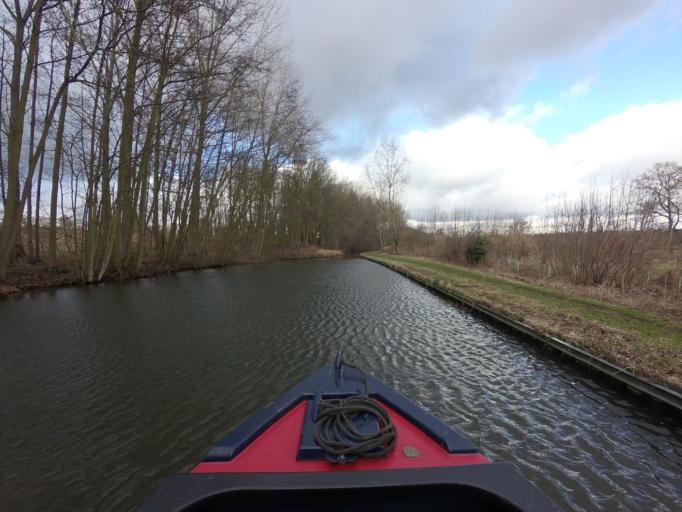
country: GB
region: England
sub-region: Northamptonshire
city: Long Buckby
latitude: 52.2542
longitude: -1.0848
